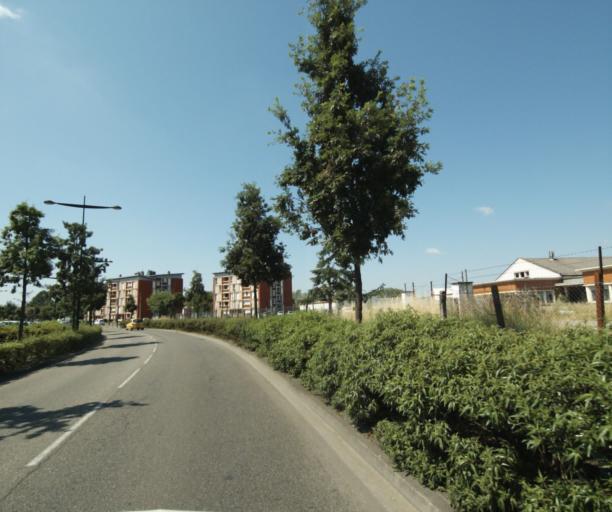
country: FR
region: Midi-Pyrenees
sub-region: Departement du Tarn-et-Garonne
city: Montauban
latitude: 44.0264
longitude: 1.3425
